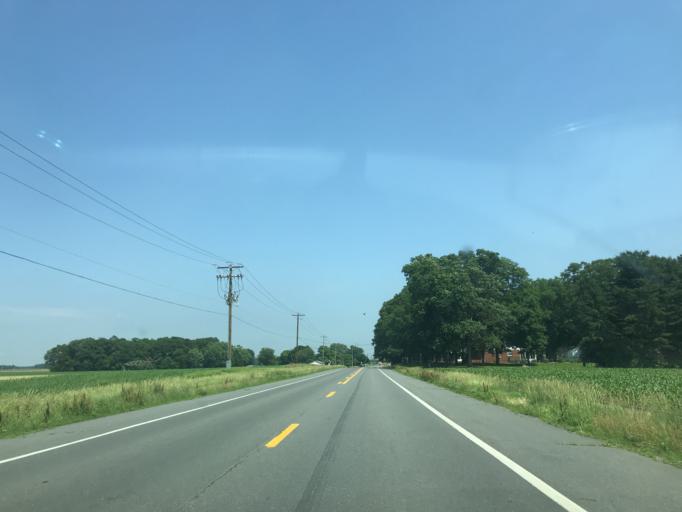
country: US
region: Maryland
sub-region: Dorchester County
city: Hurlock
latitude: 38.5905
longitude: -75.8772
